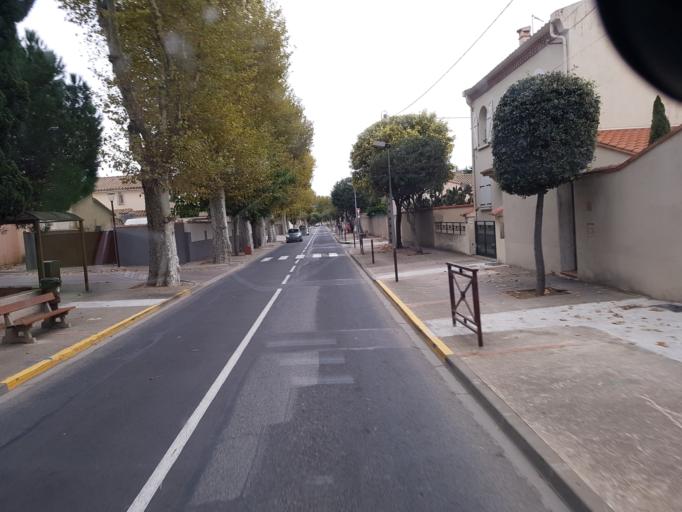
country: FR
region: Languedoc-Roussillon
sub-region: Departement des Pyrenees-Orientales
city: Torreilles
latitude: 42.7589
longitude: 2.9908
